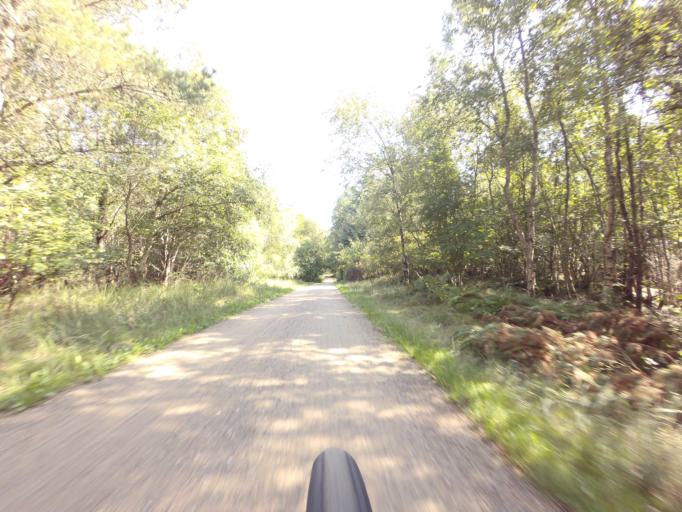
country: DK
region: North Denmark
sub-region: Hjorring Kommune
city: Hirtshals
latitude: 57.5834
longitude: 10.0705
